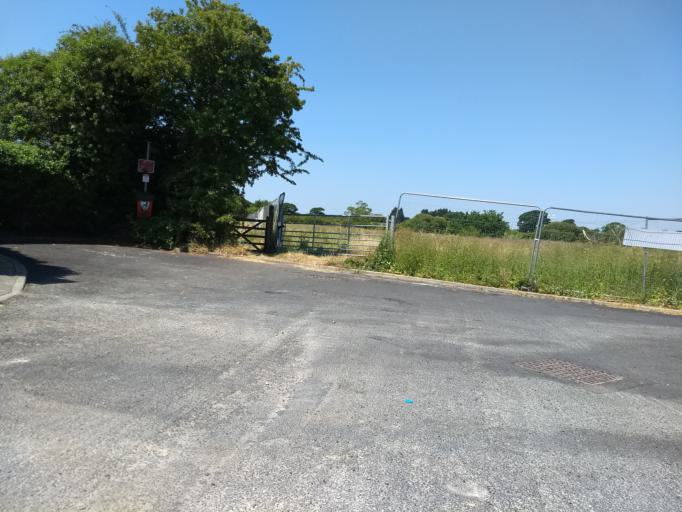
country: GB
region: England
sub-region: Isle of Wight
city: Newport
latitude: 50.6999
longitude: -1.3249
